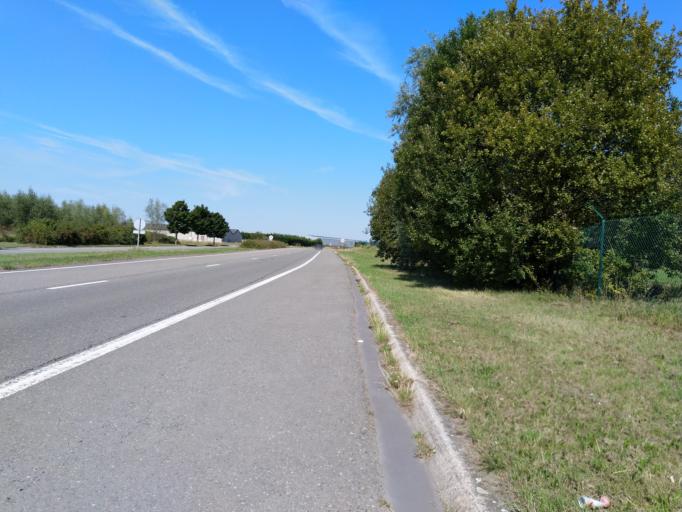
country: BE
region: Wallonia
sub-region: Province du Hainaut
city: Roeulx
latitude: 50.4868
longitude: 4.1150
